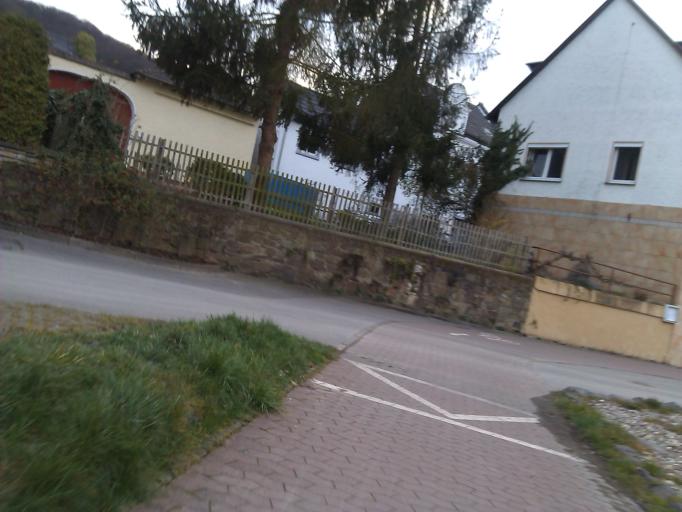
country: DE
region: North Rhine-Westphalia
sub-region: Regierungsbezirk Koln
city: Bad Honnef
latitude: 50.6449
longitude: 7.2065
